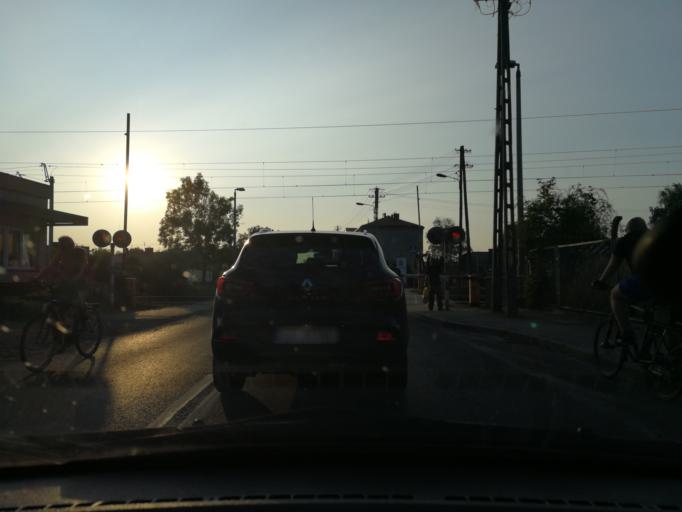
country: PL
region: Lodz Voivodeship
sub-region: Skierniewice
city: Skierniewice
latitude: 51.9612
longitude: 20.1354
